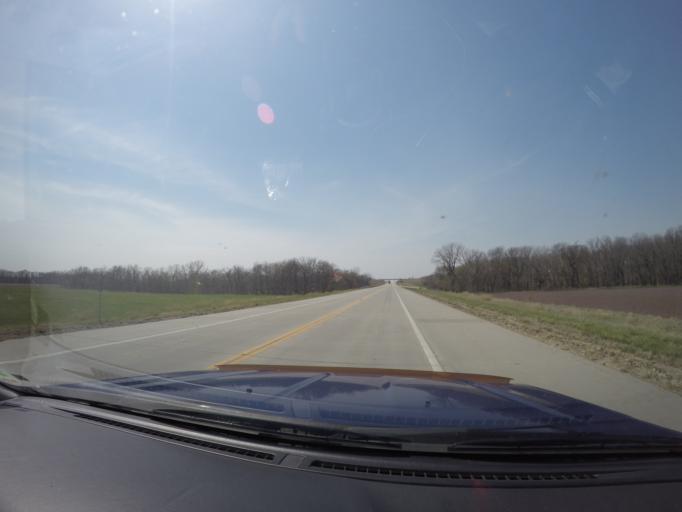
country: US
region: Kansas
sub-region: Chase County
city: Cottonwood Falls
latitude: 38.4001
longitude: -96.5457
